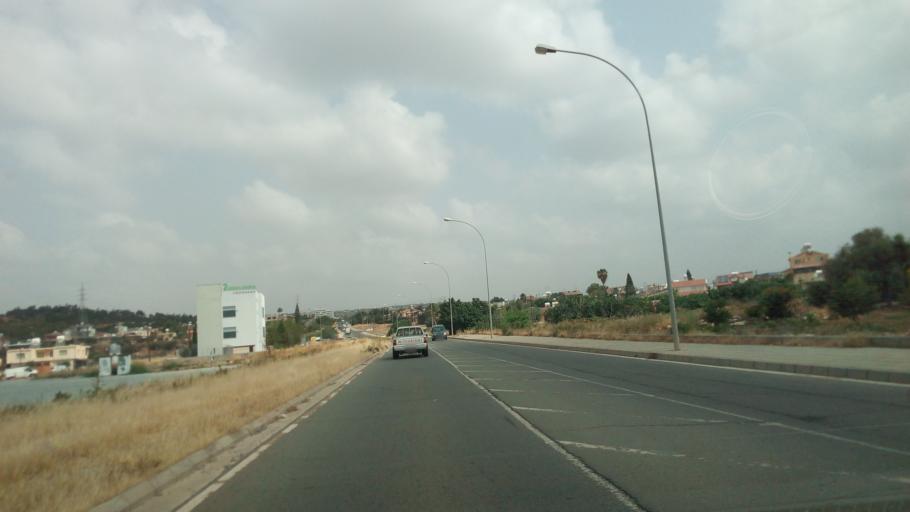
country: CY
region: Limassol
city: Pano Polemidia
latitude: 34.6938
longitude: 32.9884
